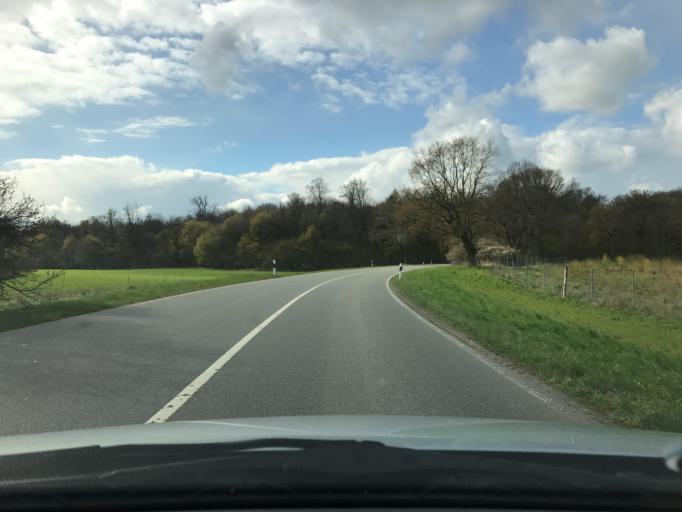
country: DE
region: Schleswig-Holstein
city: Schonwalde am Bungsberg
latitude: 54.1749
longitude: 10.7772
